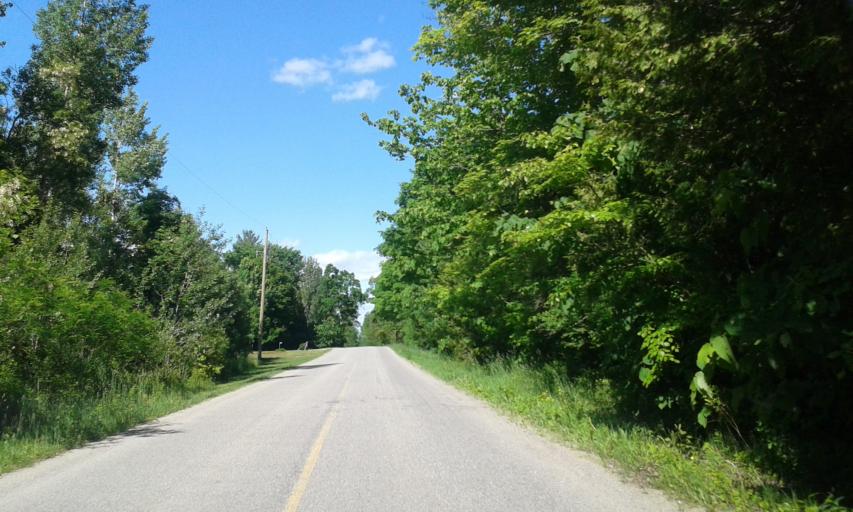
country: CA
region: Ontario
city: Brockville
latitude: 44.6278
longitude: -75.7379
